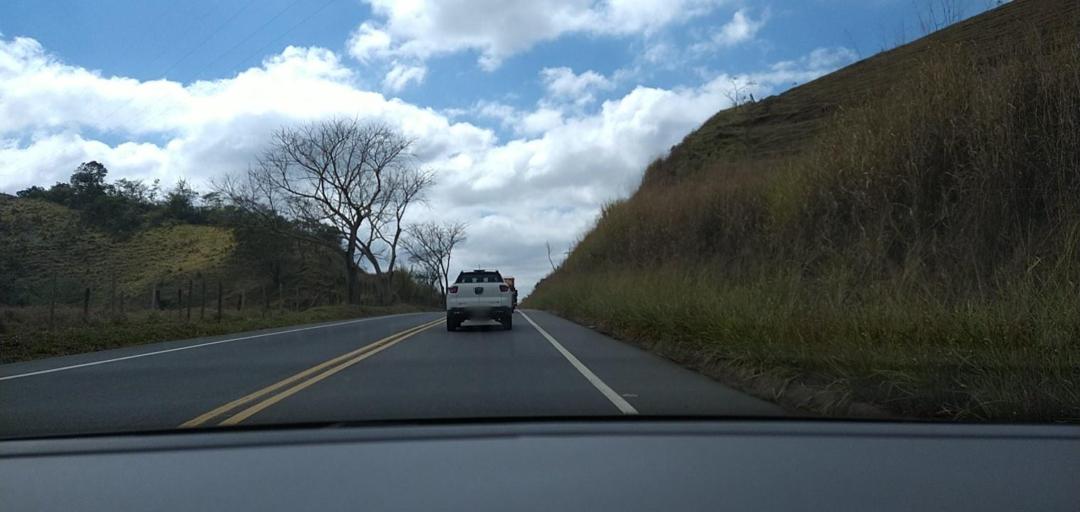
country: BR
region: Minas Gerais
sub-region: Ponte Nova
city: Ponte Nova
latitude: -20.5123
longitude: -42.8872
